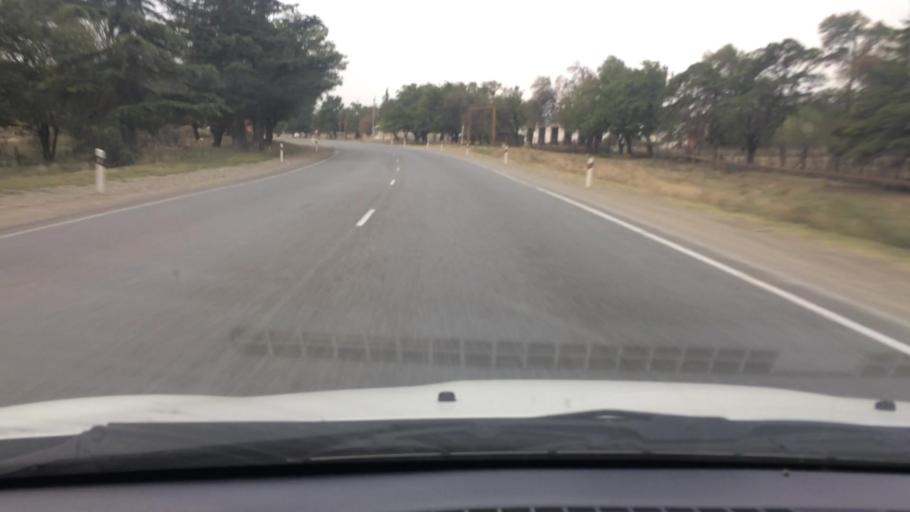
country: GE
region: T'bilisi
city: Tbilisi
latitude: 41.6431
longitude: 44.8399
